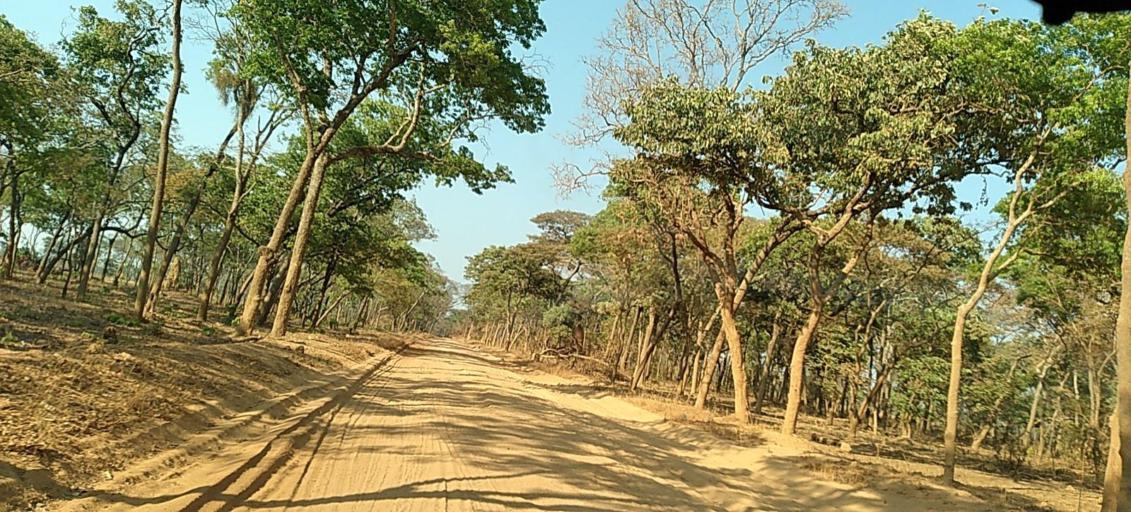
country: ZM
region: North-Western
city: Kasempa
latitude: -13.5901
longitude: 25.9844
